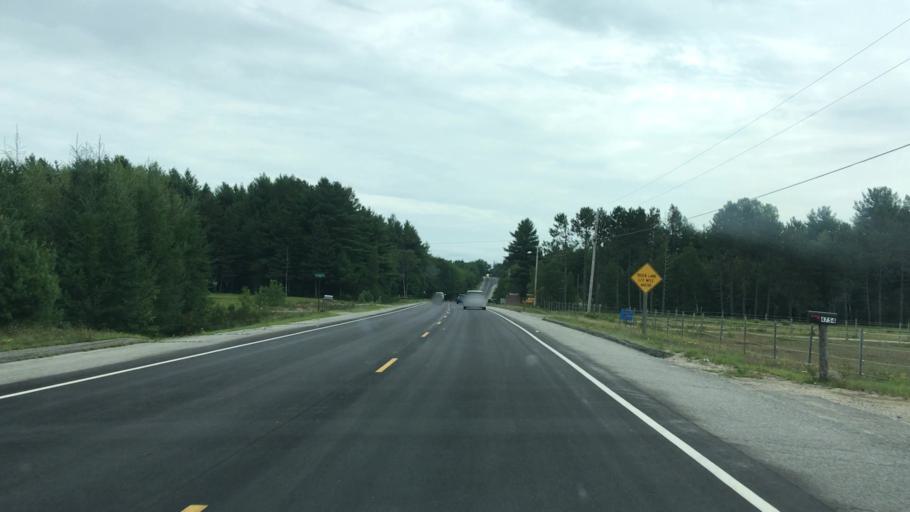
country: US
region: Maine
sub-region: Washington County
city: Addison
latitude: 44.9420
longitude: -67.7130
